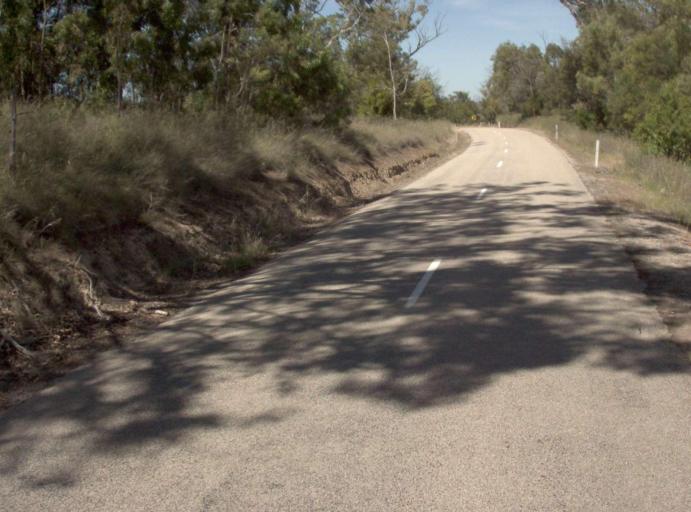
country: AU
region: Victoria
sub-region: East Gippsland
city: Lakes Entrance
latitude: -37.4631
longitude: 148.1947
